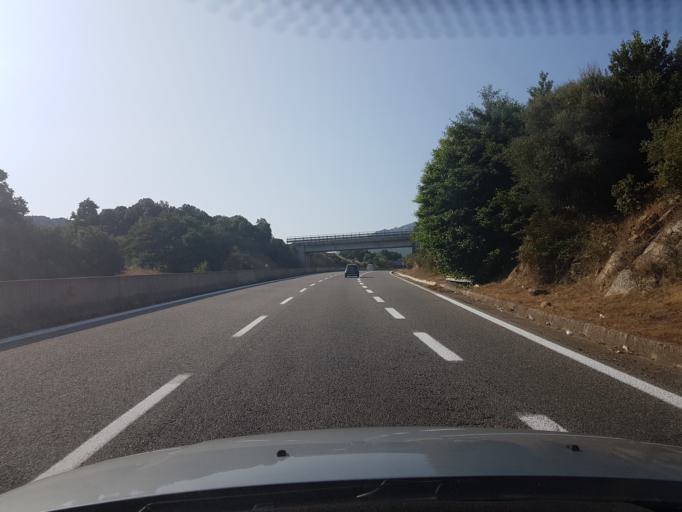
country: IT
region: Sardinia
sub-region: Provincia di Olbia-Tempio
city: Padru
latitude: 40.8094
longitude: 9.5903
